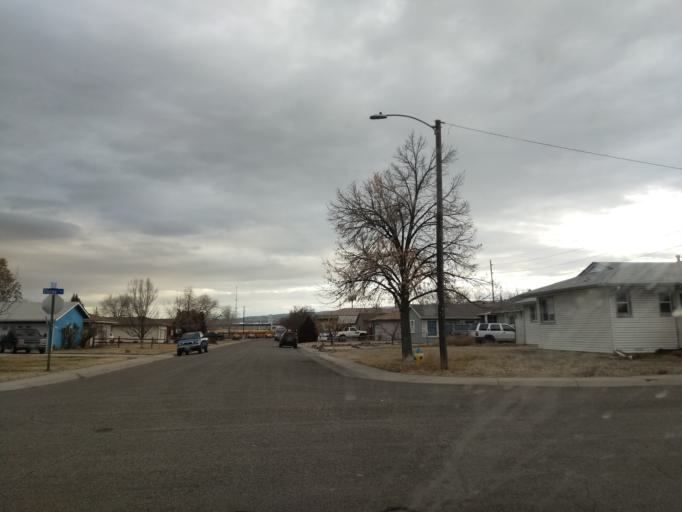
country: US
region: Colorado
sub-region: Mesa County
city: Grand Junction
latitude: 39.0717
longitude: -108.5385
